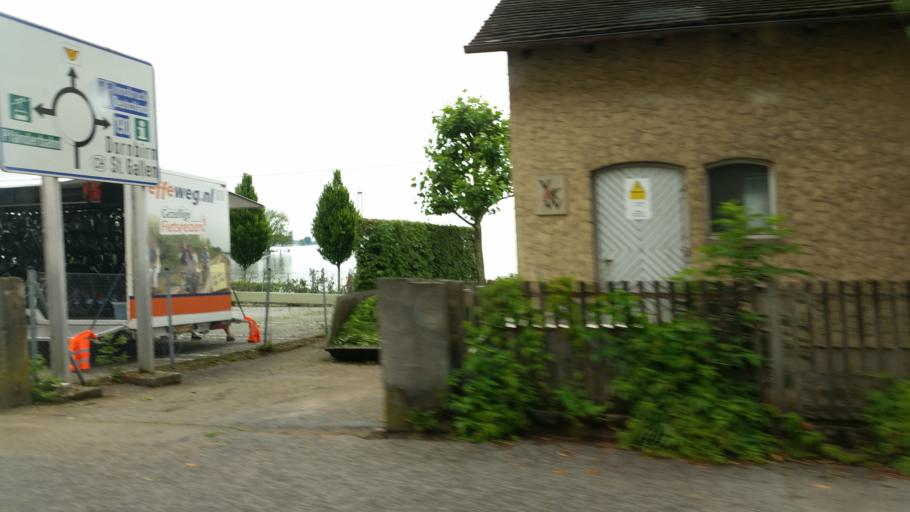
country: AT
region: Vorarlberg
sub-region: Politischer Bezirk Bregenz
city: Bregenz
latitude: 47.5084
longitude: 9.7516
